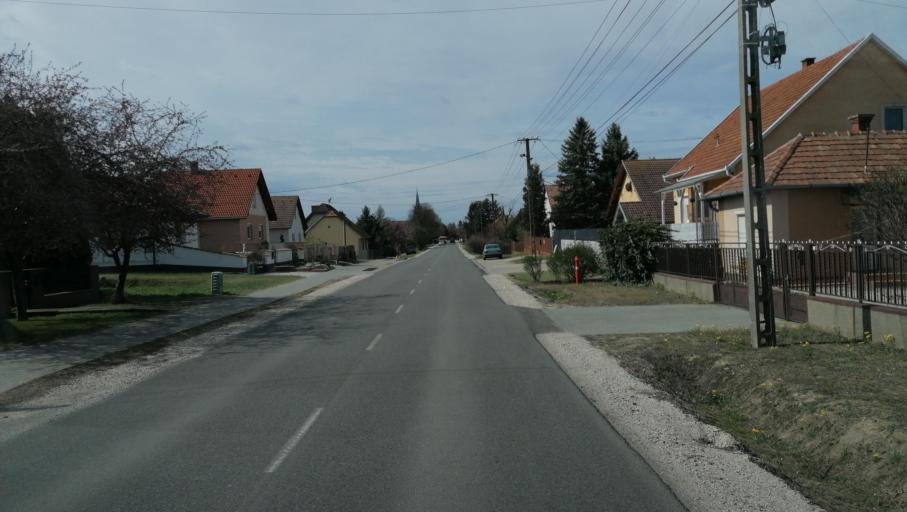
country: HU
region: Pest
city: Dabas
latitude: 47.1753
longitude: 19.3367
